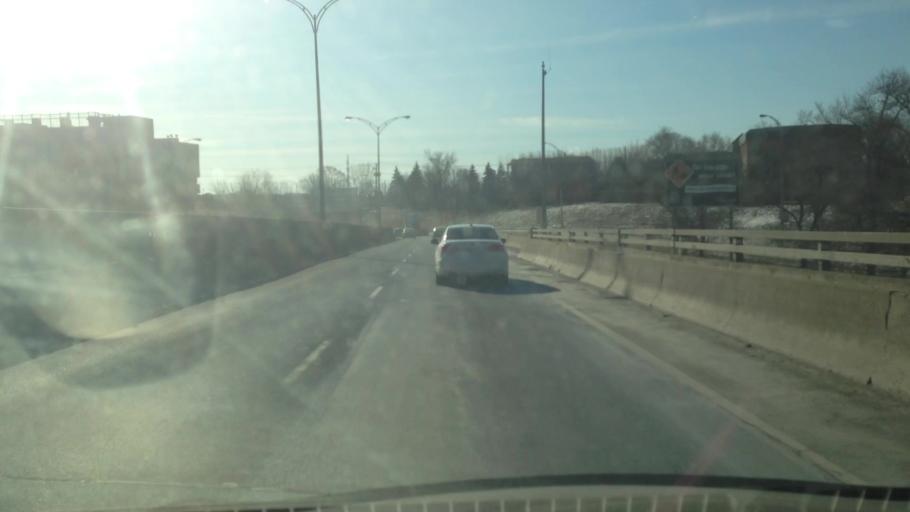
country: CA
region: Quebec
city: Montreal-Ouest
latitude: 45.4339
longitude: -73.6504
